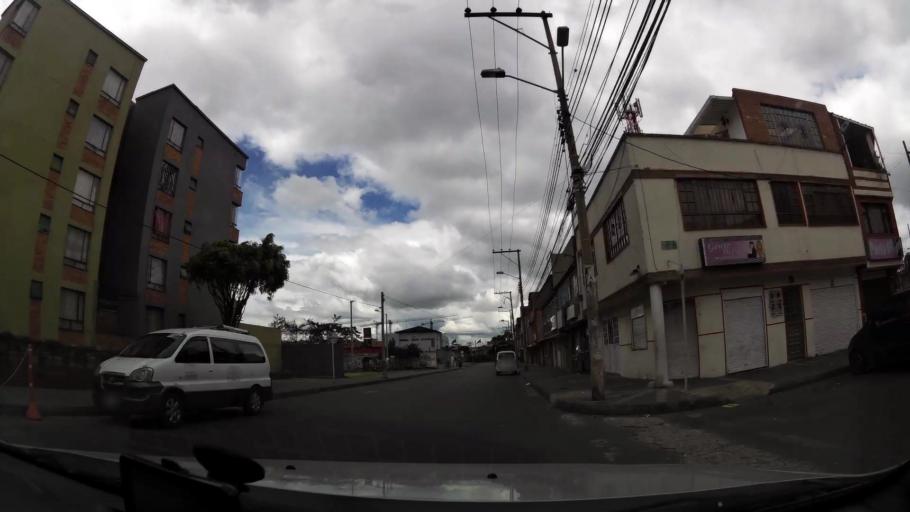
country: CO
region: Bogota D.C.
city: Bogota
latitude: 4.6224
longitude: -74.1237
